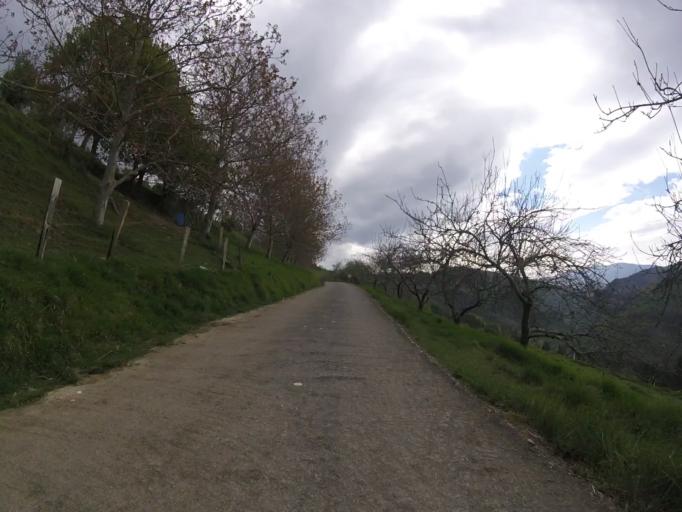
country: ES
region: Basque Country
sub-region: Provincia de Guipuzcoa
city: Aizarnazabal
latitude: 43.2547
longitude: -2.2197
